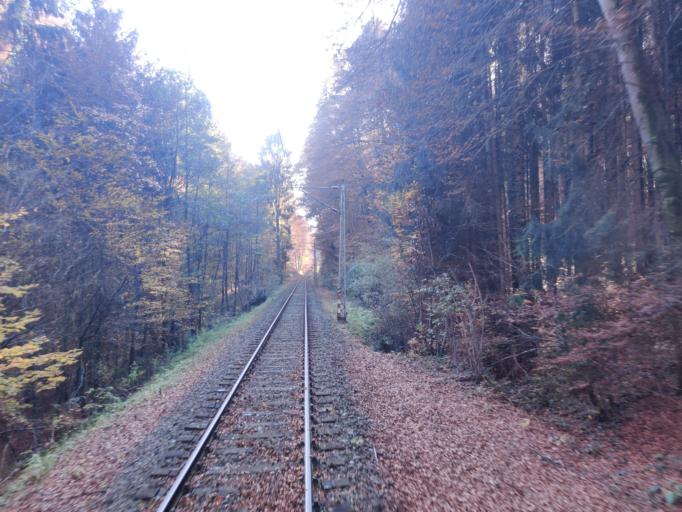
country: AT
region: Styria
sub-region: Politischer Bezirk Suedoststeiermark
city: Maierdorf
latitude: 46.9189
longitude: 15.8425
